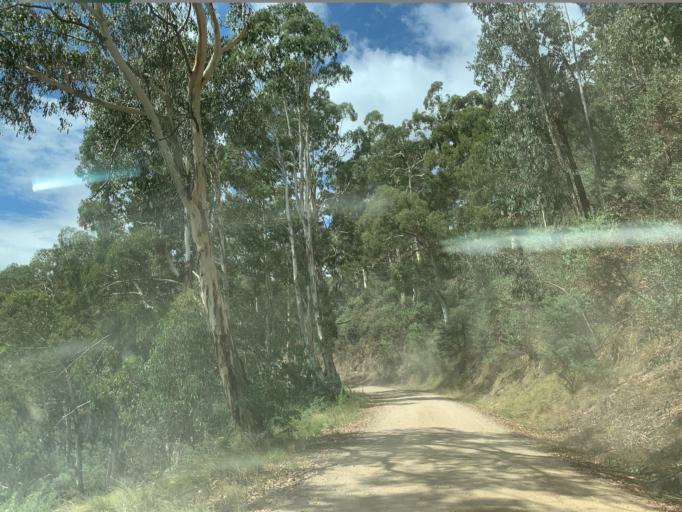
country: AU
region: Victoria
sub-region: Mansfield
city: Mansfield
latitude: -37.0927
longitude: 146.5363
